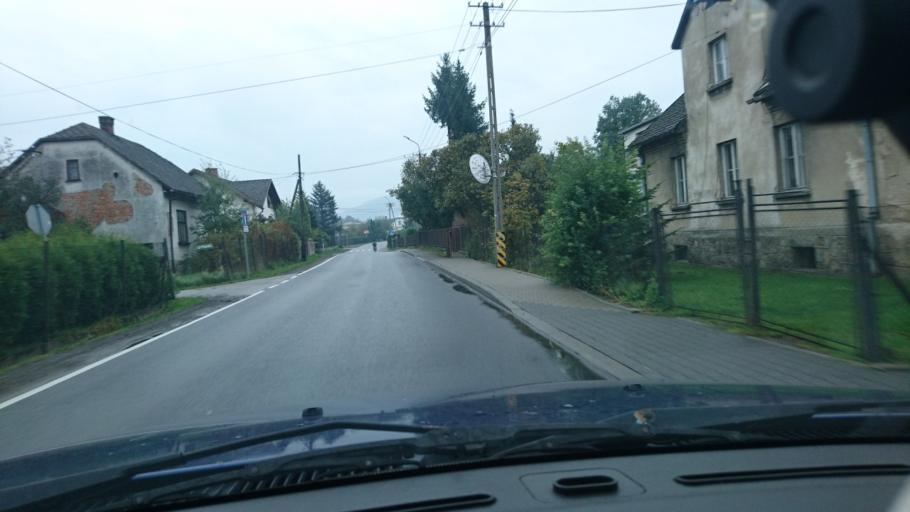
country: PL
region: Silesian Voivodeship
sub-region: Powiat bielski
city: Kozy
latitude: 49.8537
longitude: 19.1393
